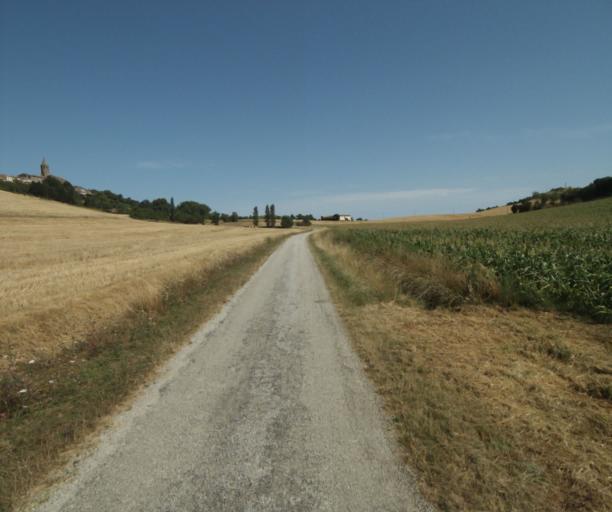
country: FR
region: Midi-Pyrenees
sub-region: Departement de la Haute-Garonne
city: Saint-Felix-Lauragais
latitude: 43.4490
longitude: 1.8793
